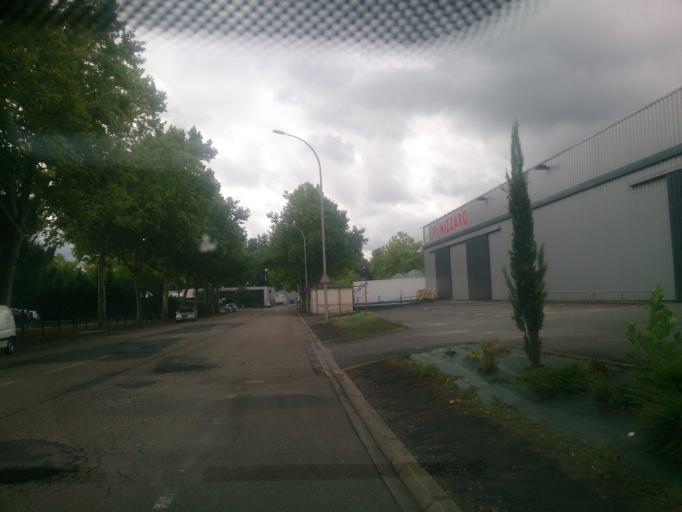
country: FR
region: Limousin
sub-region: Departement de la Correze
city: Ussac
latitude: 45.1614
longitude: 1.4866
